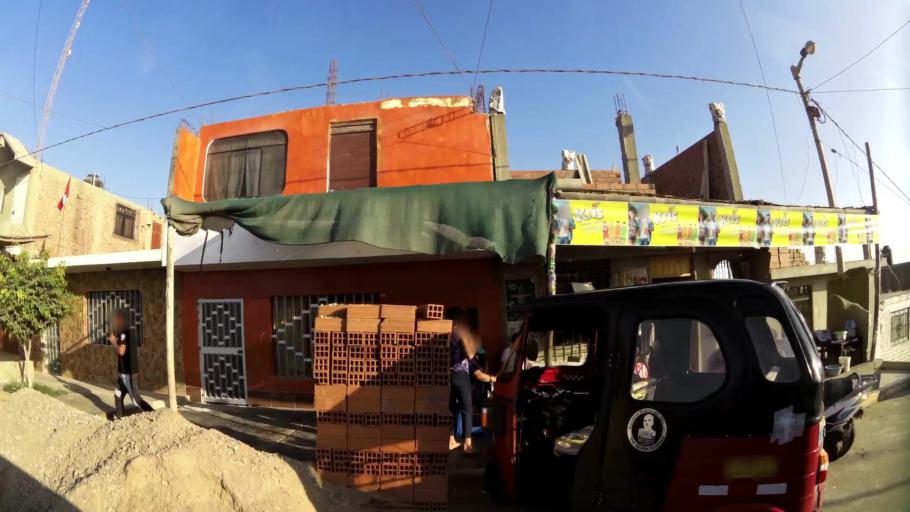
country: PE
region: Ica
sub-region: Provincia de Pisco
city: Villa Tupac Amaru
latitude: -13.7053
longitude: -76.1476
